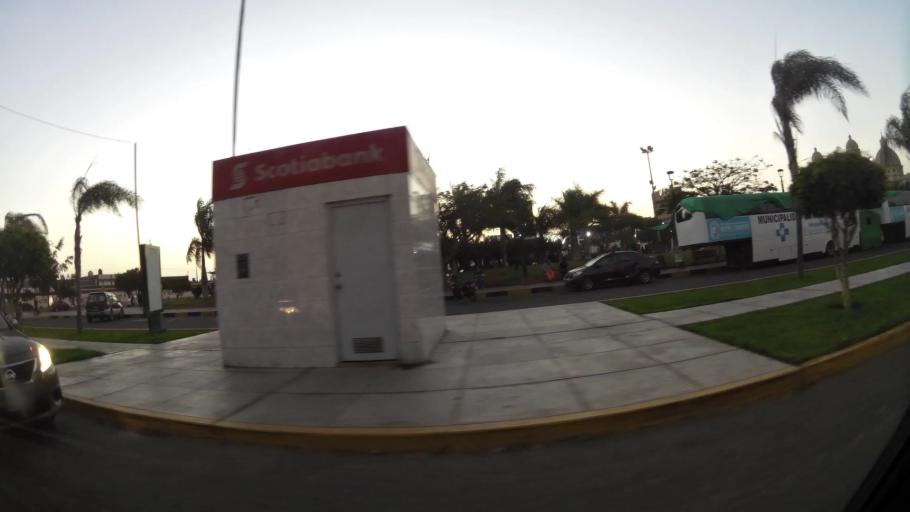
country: PE
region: Ancash
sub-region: Provincia de Santa
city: Buenos Aires
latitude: -9.1227
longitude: -78.5303
